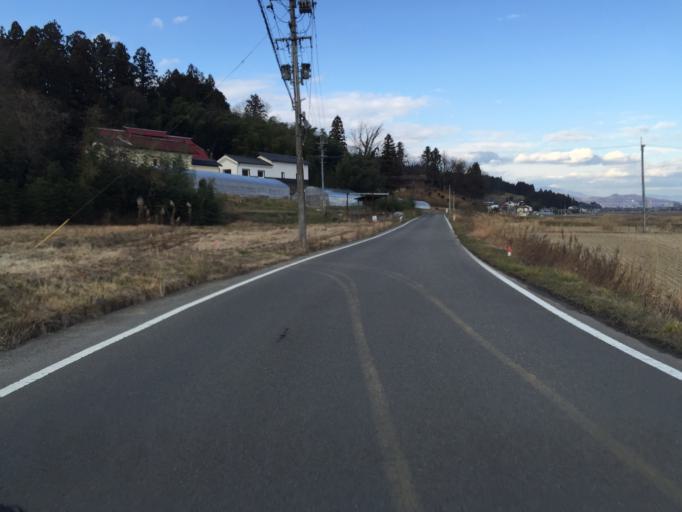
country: JP
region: Fukushima
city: Fukushima-shi
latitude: 37.6921
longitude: 140.4419
